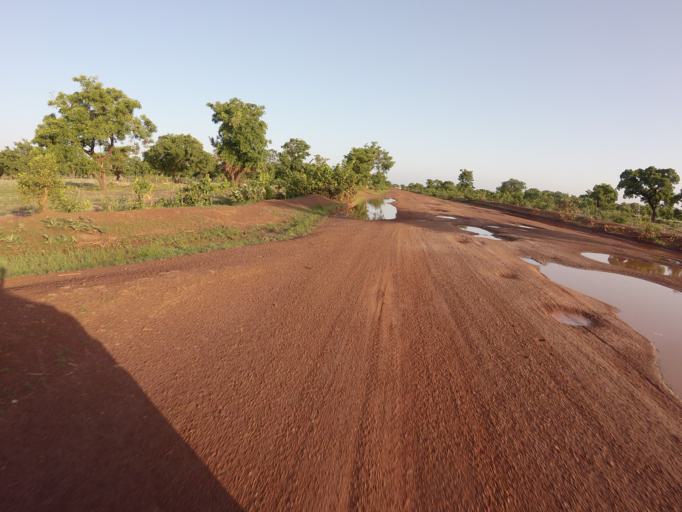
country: TG
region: Savanes
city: Sansanne-Mango
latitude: 10.2754
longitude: -0.0828
